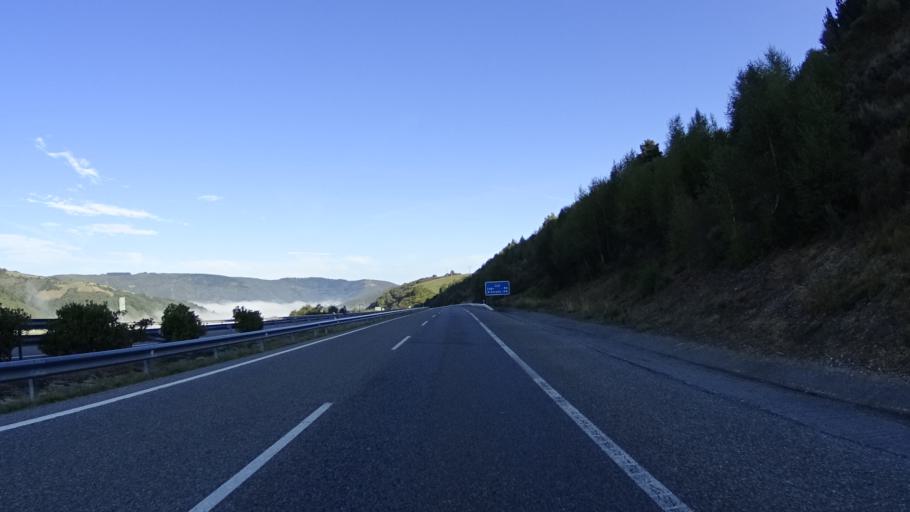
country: ES
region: Galicia
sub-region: Provincia de Lugo
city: San Roman
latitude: 42.7674
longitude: -7.0870
